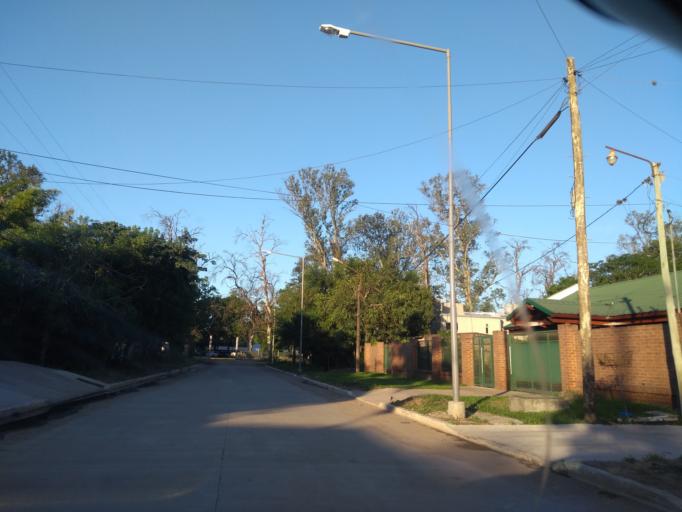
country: AR
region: Chaco
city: Resistencia
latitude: -27.4676
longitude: -58.9586
